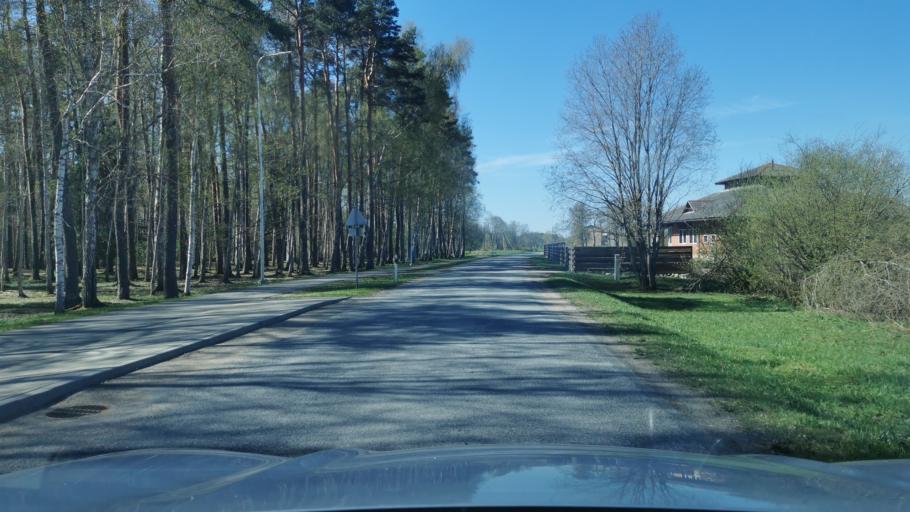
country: EE
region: Laeaene-Virumaa
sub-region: Rakke vald
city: Rakke
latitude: 59.0447
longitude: 26.3994
